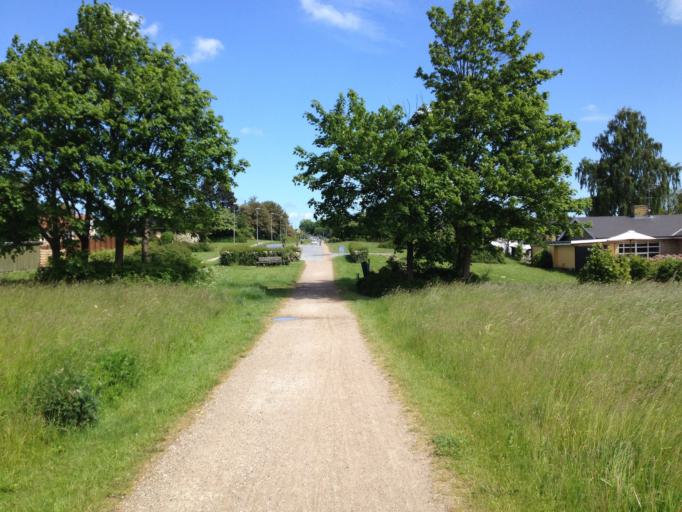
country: DK
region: Capital Region
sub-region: Fredensborg Kommune
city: Niva
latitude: 55.9312
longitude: 12.4902
